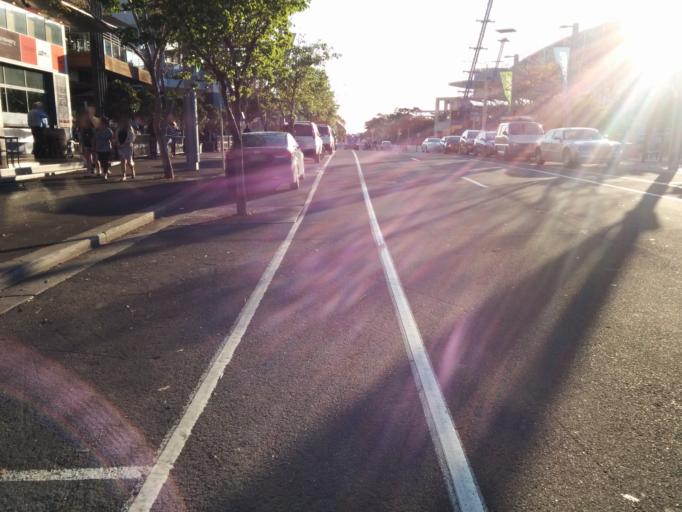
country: AU
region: New South Wales
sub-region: Canada Bay
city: Concord West
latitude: -33.8476
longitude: 151.0677
